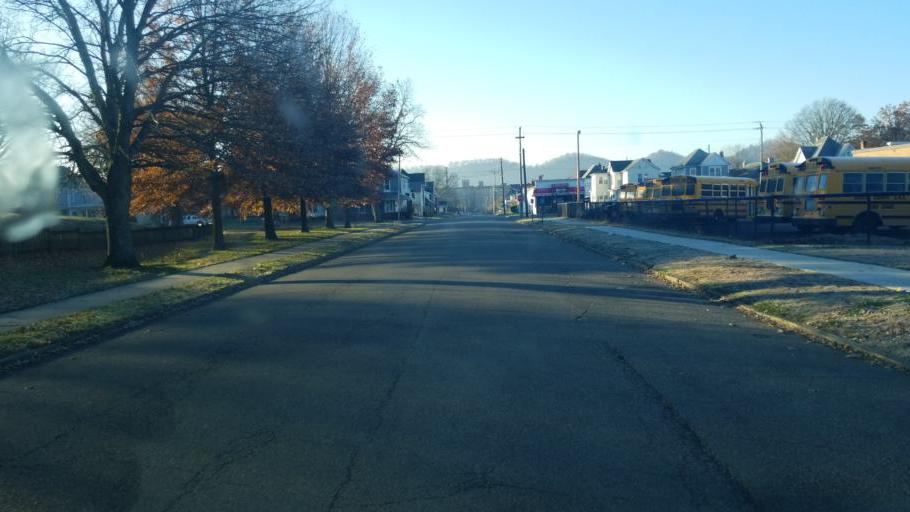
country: US
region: Ohio
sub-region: Scioto County
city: Portsmouth
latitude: 38.7434
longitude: -82.9782
